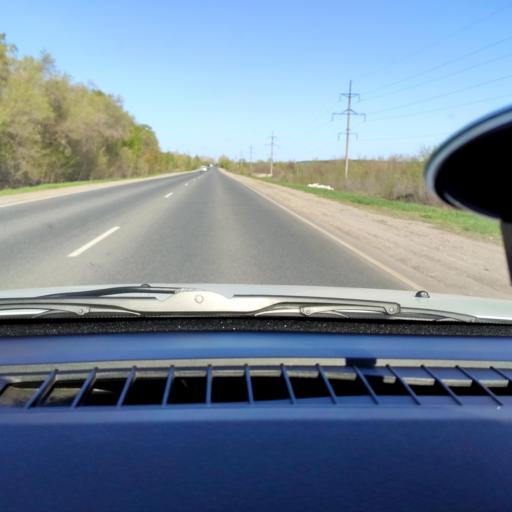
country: RU
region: Samara
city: Dubovyy Umet
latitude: 53.1012
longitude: 50.2546
